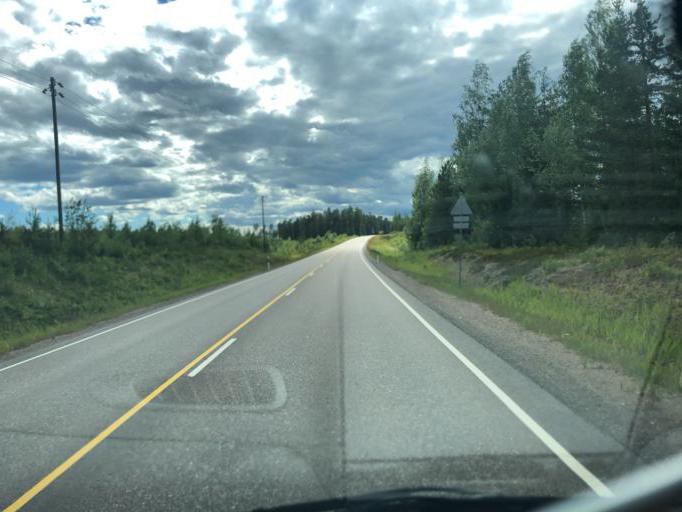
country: FI
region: Southern Savonia
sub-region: Mikkeli
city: Maentyharju
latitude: 61.0964
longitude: 27.0879
